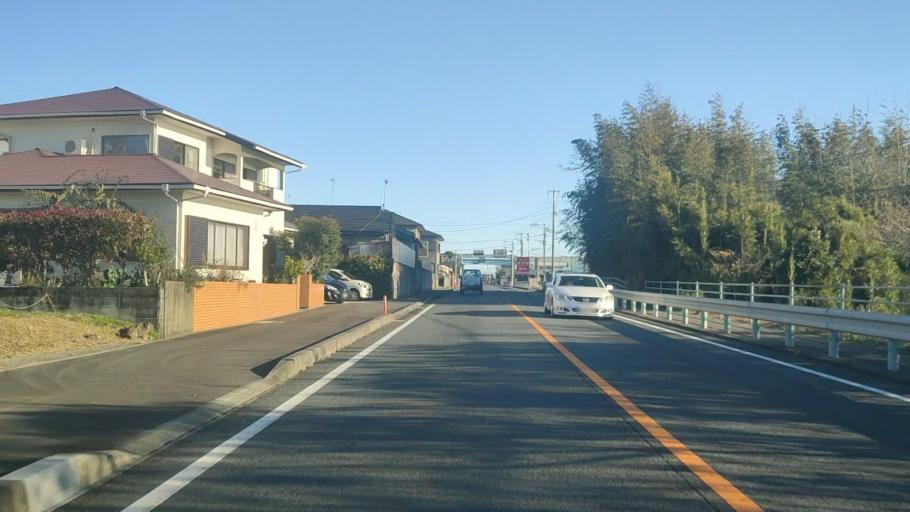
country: JP
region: Miyazaki
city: Nobeoka
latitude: 32.3684
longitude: 131.6279
